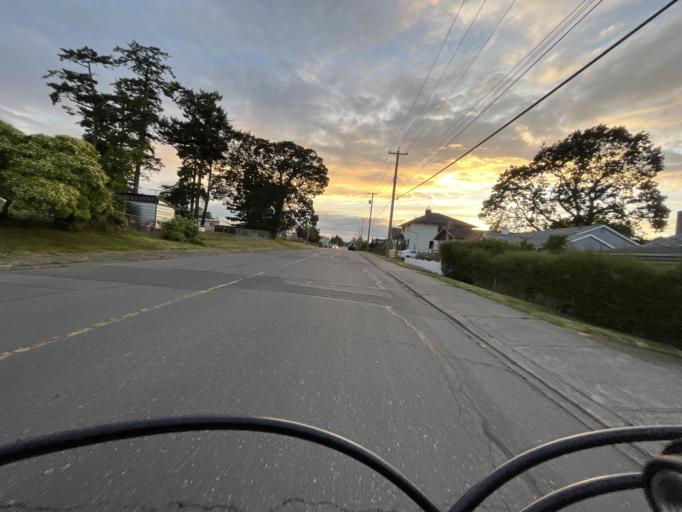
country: CA
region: British Columbia
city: Victoria
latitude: 48.4266
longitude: -123.4026
